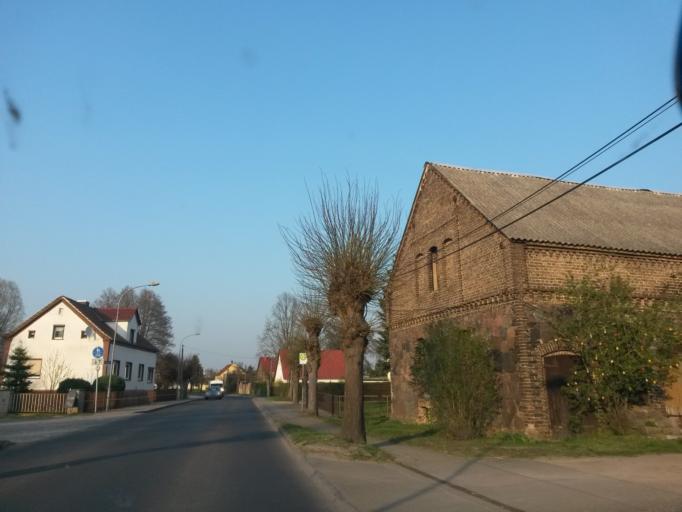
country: DE
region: Brandenburg
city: Rehfelde
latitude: 52.5034
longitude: 13.9260
